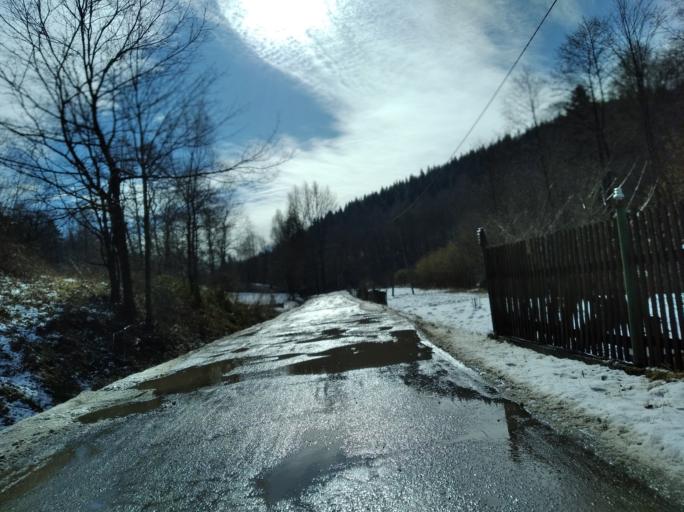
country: PL
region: Subcarpathian Voivodeship
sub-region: Powiat brzozowski
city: Jablonica Polska
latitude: 49.7389
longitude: 21.8866
